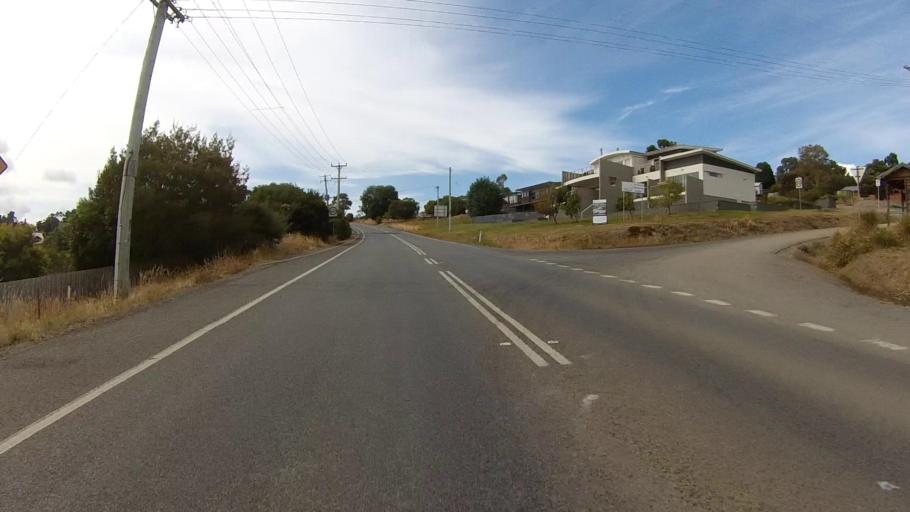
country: AU
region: Tasmania
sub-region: Kingborough
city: Kettering
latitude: -43.1286
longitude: 147.2469
